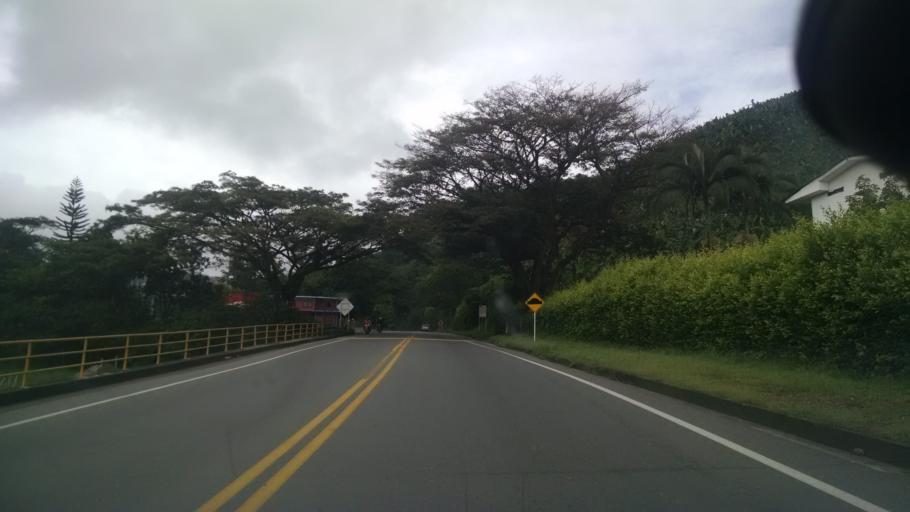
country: CO
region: Caldas
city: Palestina
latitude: 5.0710
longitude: -75.6298
